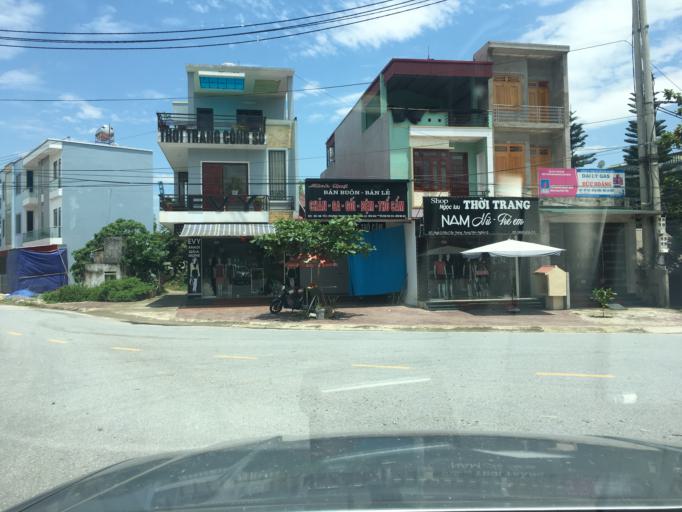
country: VN
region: Yen Bai
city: Son Thinh
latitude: 21.6104
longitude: 104.5063
